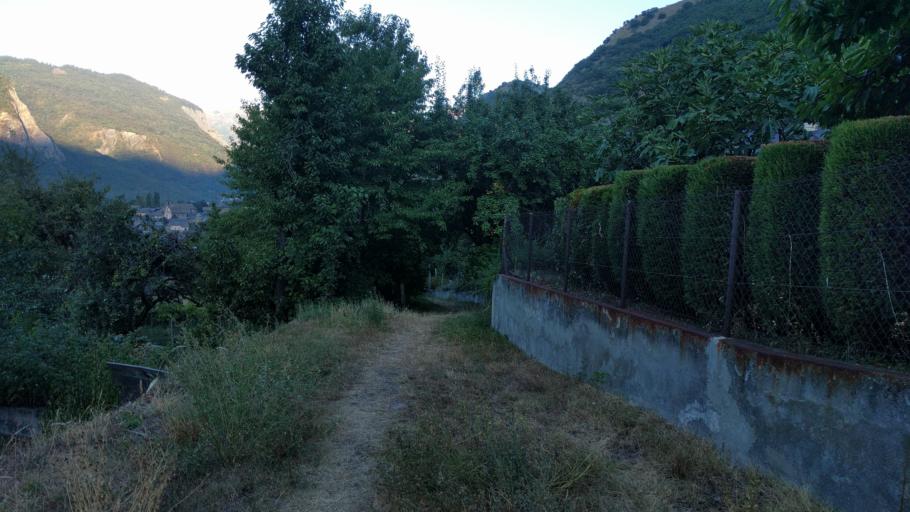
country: FR
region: Rhone-Alpes
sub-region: Departement de la Savoie
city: Villargondran
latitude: 45.2557
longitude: 6.4141
